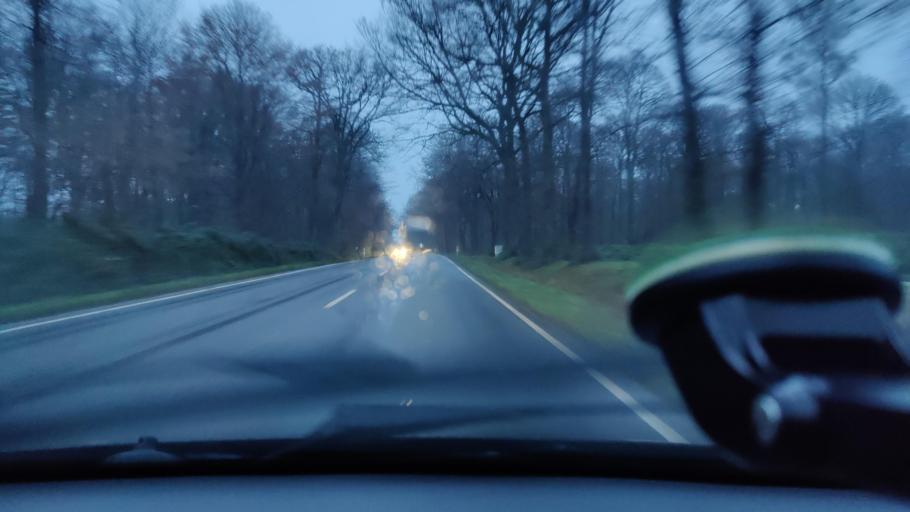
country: DE
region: North Rhine-Westphalia
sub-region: Regierungsbezirk Dusseldorf
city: Sonsbeck
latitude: 51.5916
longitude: 6.3859
